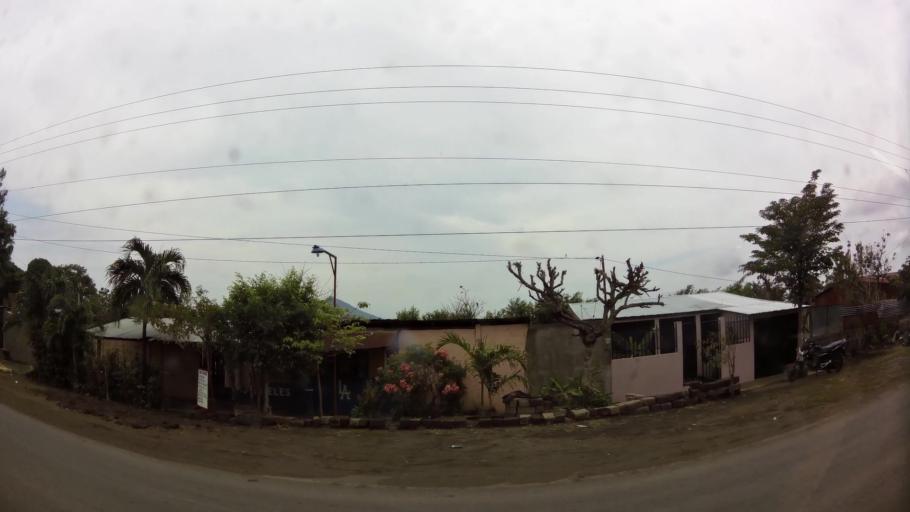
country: NI
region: Granada
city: Nandaime
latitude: 11.7638
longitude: -86.0485
